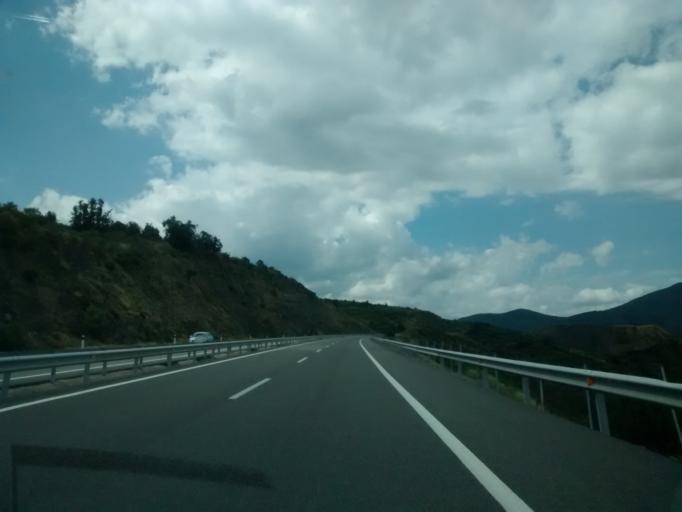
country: ES
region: Castille and Leon
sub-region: Provincia de Leon
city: Soto y Amio
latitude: 42.7985
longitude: -5.8272
